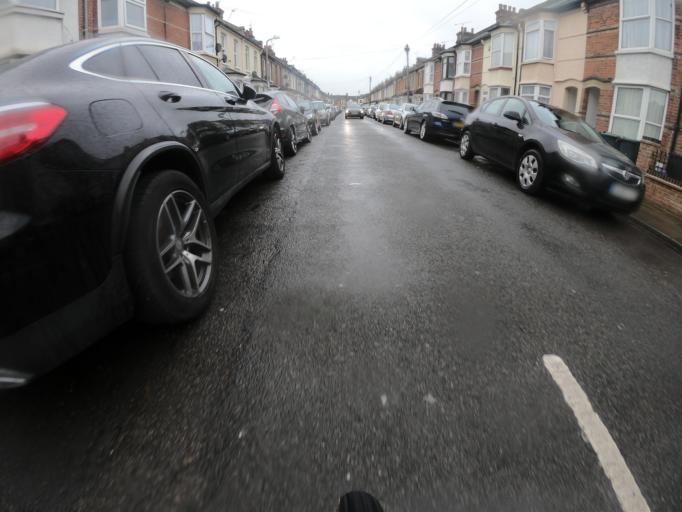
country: GB
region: England
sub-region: Kent
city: Gravesend
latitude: 51.4364
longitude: 0.3548
